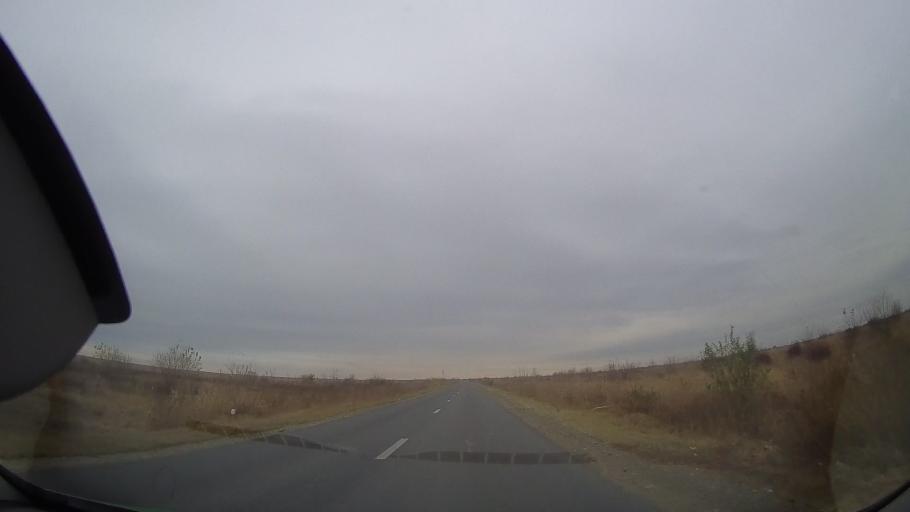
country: RO
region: Ialomita
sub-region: Oras Amara
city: Amara
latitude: 44.6277
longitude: 27.3012
